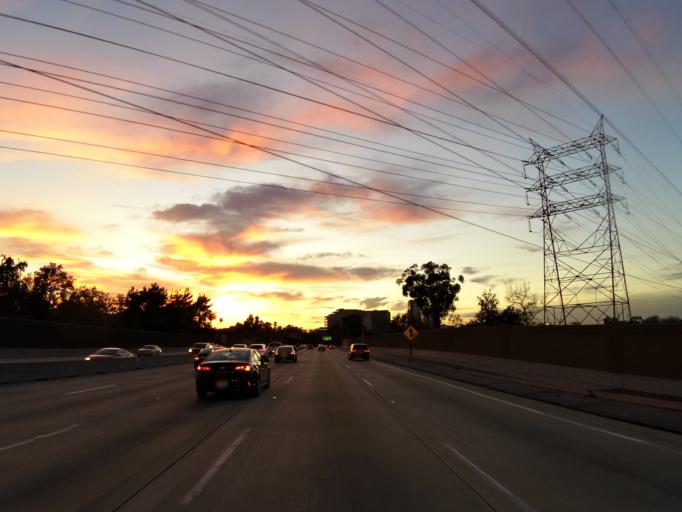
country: US
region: California
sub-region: Los Angeles County
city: Universal City
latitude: 34.1535
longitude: -118.3278
